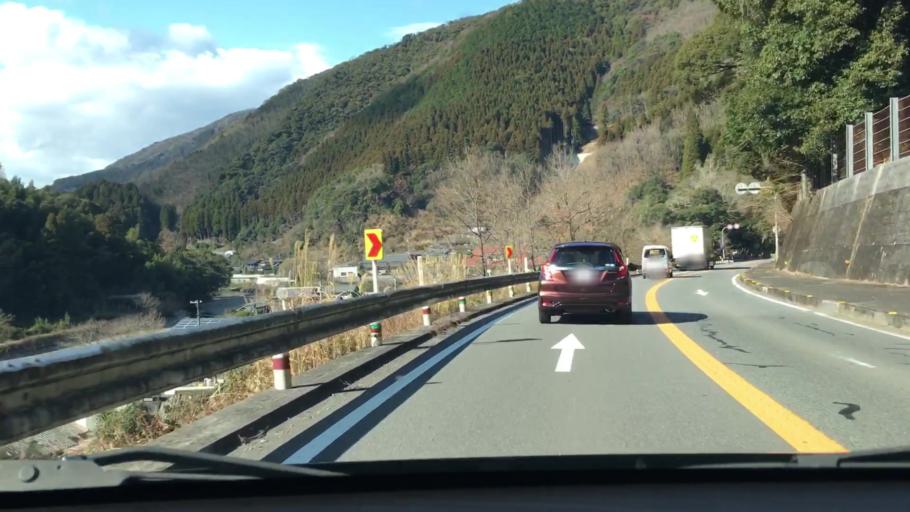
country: JP
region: Oita
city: Saiki
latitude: 32.9927
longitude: 131.8288
